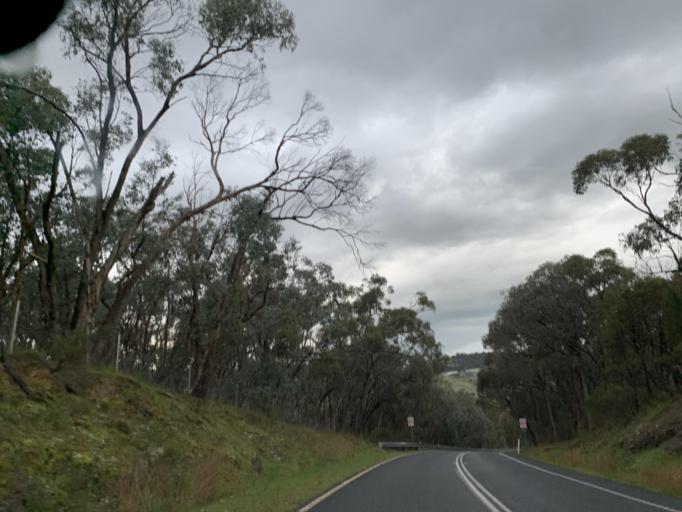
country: AU
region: Victoria
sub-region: Murrindindi
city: Kinglake West
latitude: -37.2192
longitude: 145.1328
